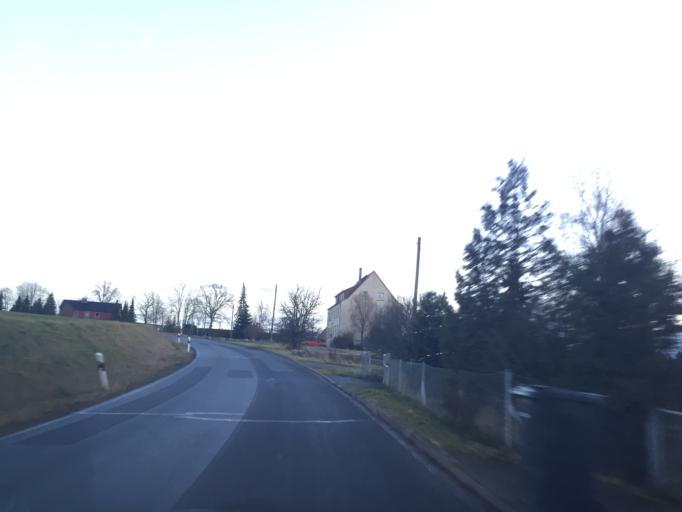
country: DE
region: Thuringia
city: Nobdenitz
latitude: 50.8777
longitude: 12.3101
